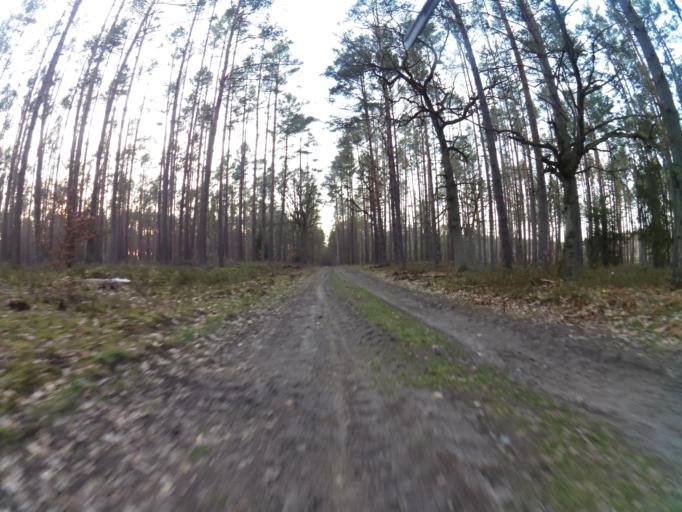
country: PL
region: West Pomeranian Voivodeship
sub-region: Powiat policki
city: Nowe Warpno
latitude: 53.6933
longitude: 14.3265
